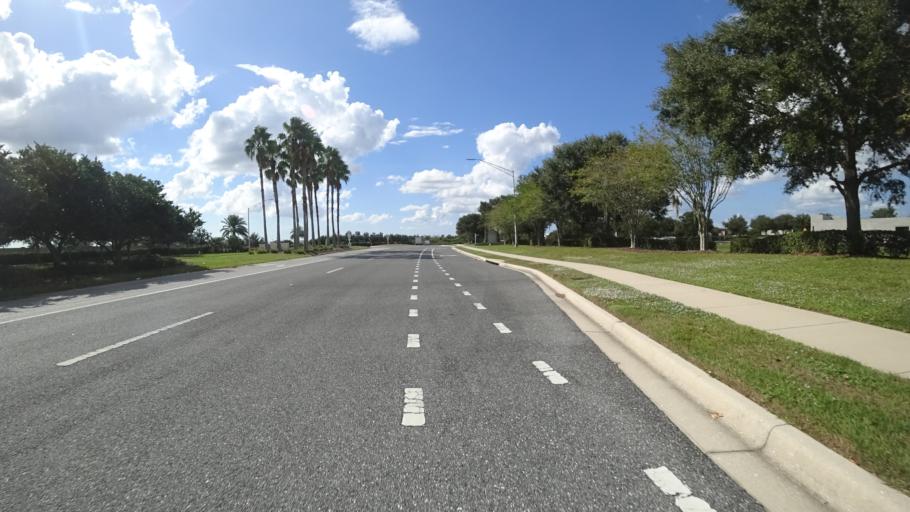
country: US
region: Florida
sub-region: Sarasota County
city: The Meadows
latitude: 27.4587
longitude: -82.4359
